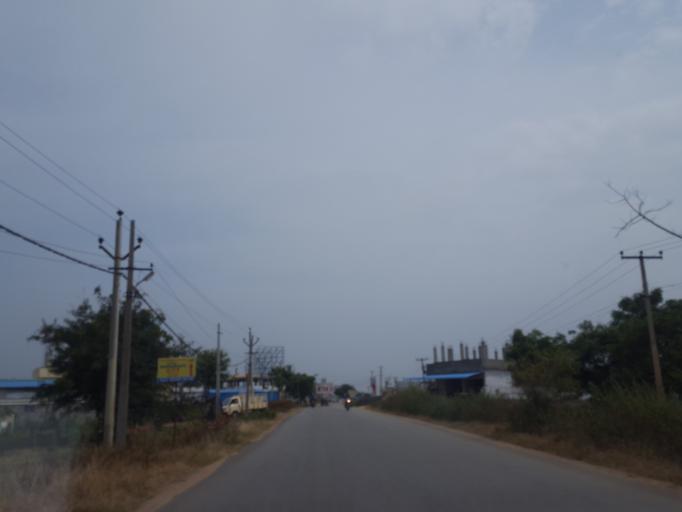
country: IN
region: Telangana
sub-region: Medak
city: Patancheru
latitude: 17.5032
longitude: 78.1984
